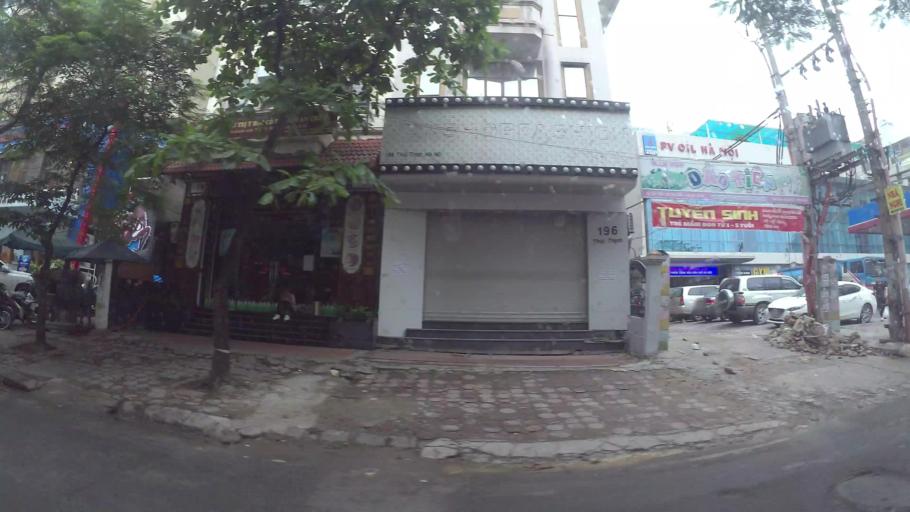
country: VN
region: Ha Noi
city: Dong Da
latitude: 21.0138
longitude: 105.8154
